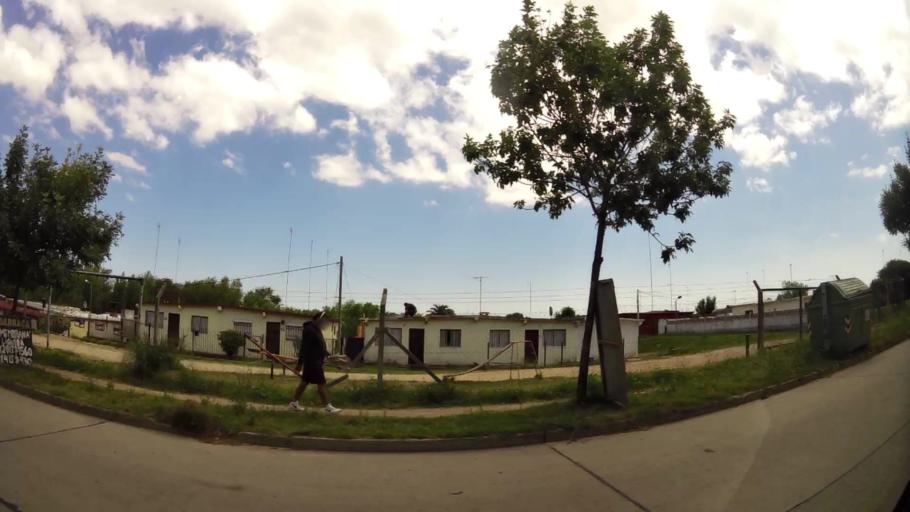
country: UY
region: Canelones
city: La Paz
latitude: -34.8319
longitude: -56.2262
